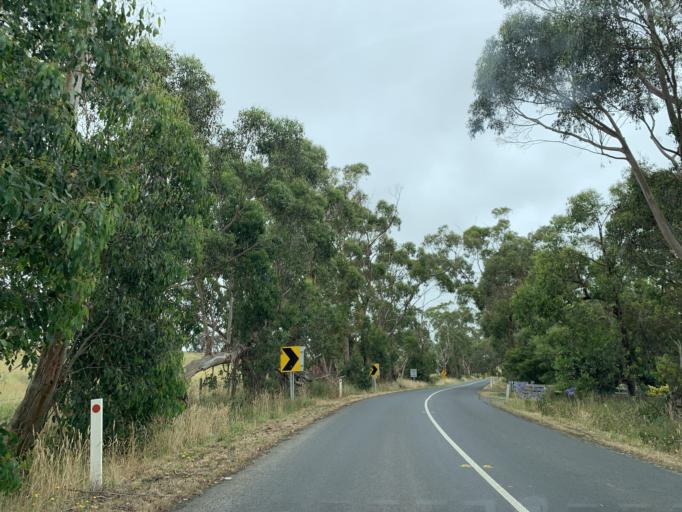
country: AU
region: Victoria
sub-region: Cardinia
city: Bunyip
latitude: -38.3308
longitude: 145.7056
